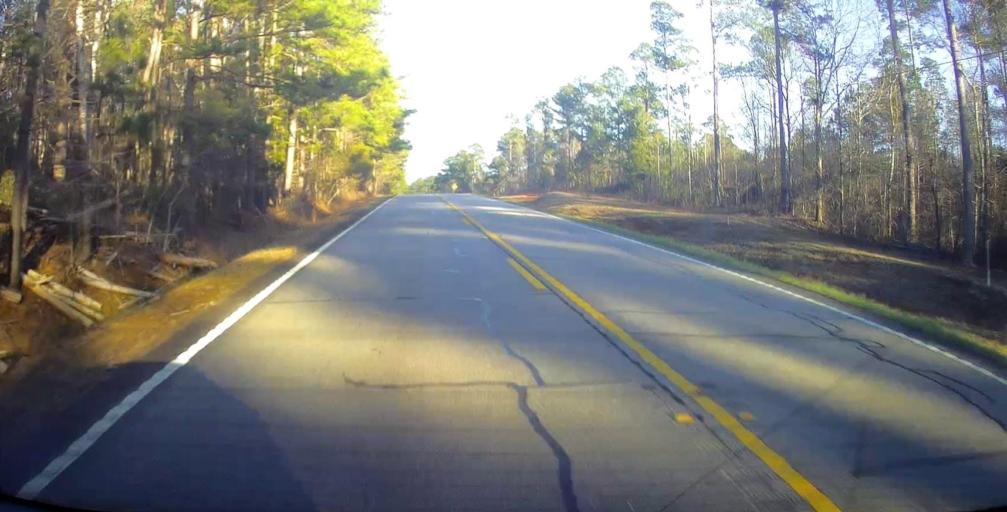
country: US
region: Georgia
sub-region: Harris County
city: Pine Mountain
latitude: 32.8444
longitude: -84.9038
